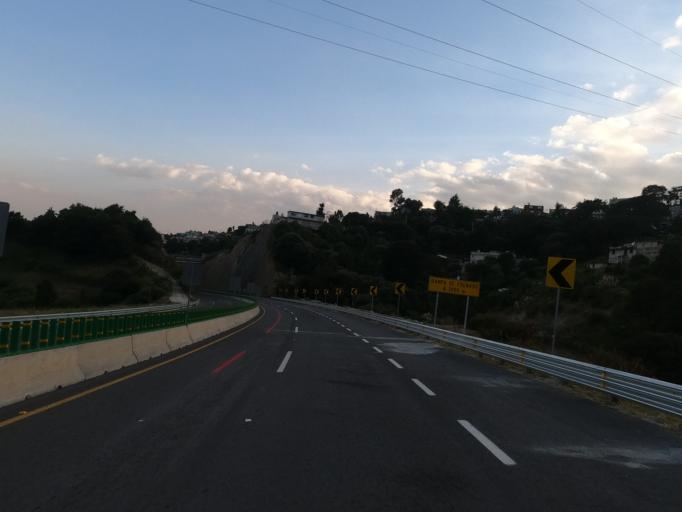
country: MX
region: Mexico
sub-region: Naucalpan de Juarez
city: Llano de las Flores (Barrio del Hueso)
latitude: 19.4263
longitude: -99.3327
